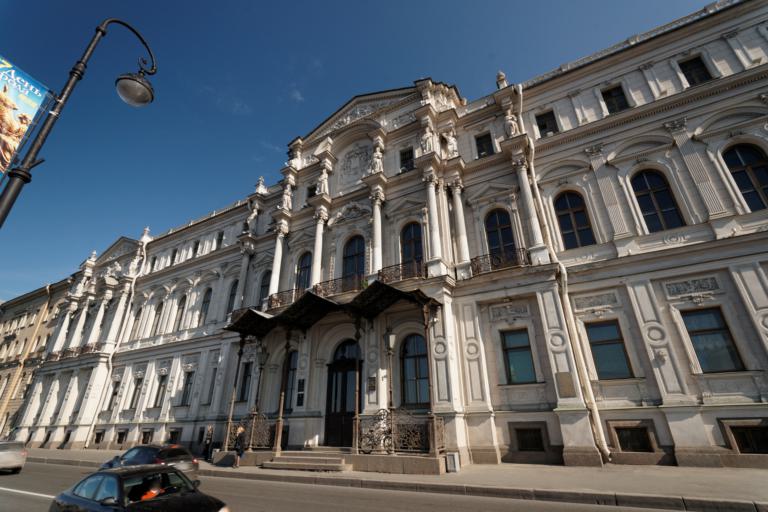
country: RU
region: St.-Petersburg
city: Saint Petersburg
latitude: 59.9442
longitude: 30.3217
